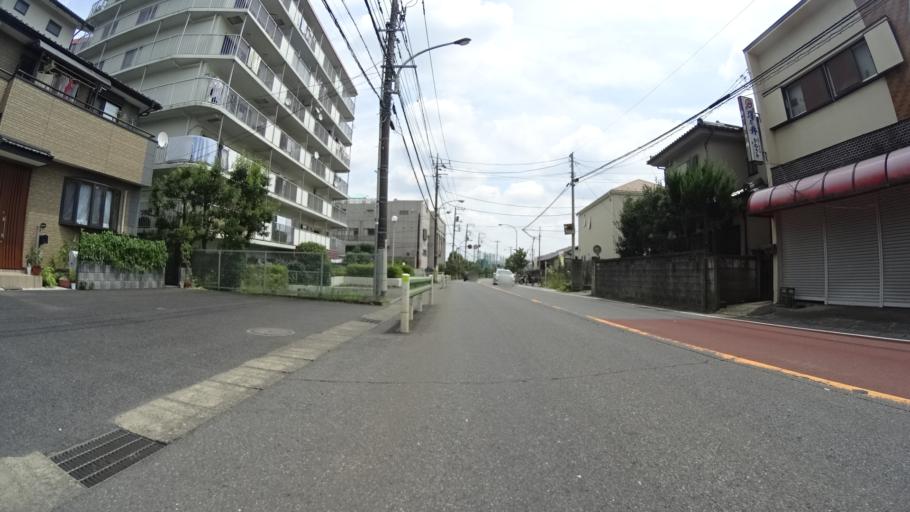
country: JP
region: Tokyo
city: Ome
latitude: 35.7808
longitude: 139.2690
